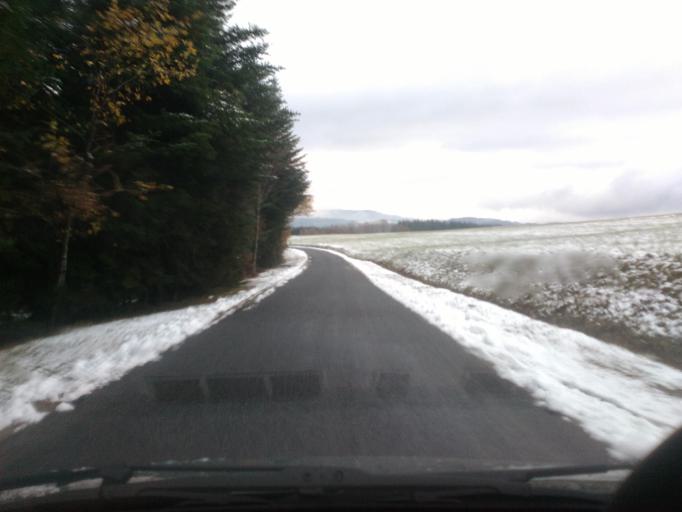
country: FR
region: Lorraine
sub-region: Departement des Vosges
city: Sainte-Marguerite
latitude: 48.2829
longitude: 7.0269
